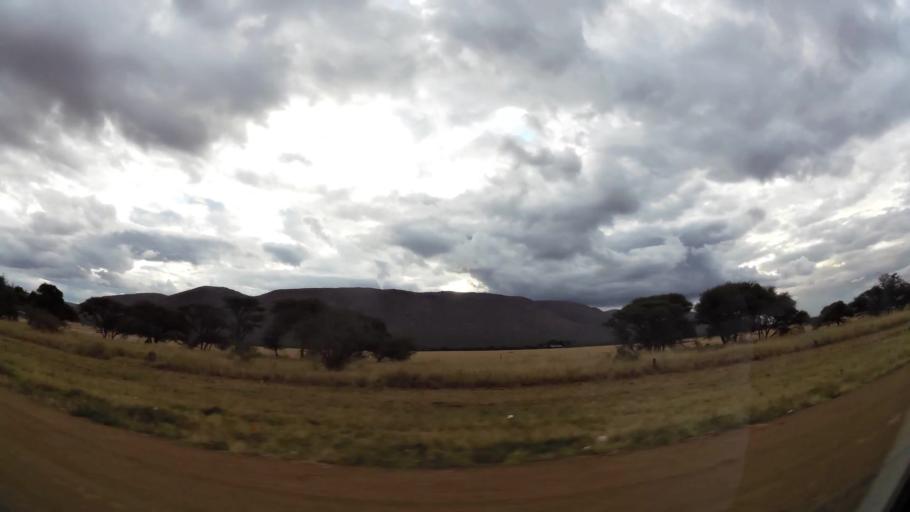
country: ZA
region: Limpopo
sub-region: Waterberg District Municipality
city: Mokopane
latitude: -24.2499
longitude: 28.9907
